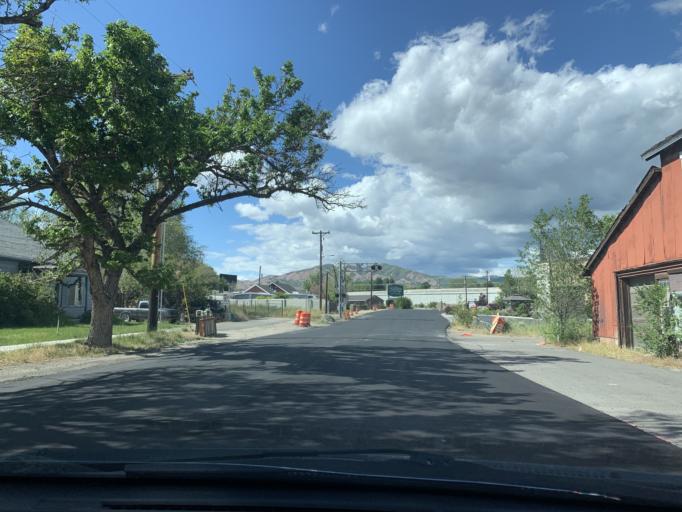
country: US
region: Utah
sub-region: Utah County
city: Lehi
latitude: 40.3977
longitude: -111.8478
